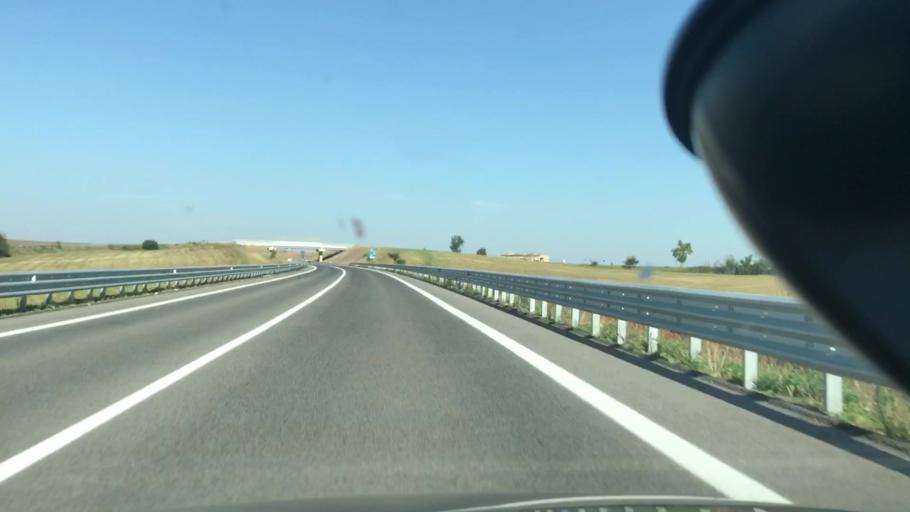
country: IT
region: Basilicate
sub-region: Provincia di Potenza
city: Palazzo San Gervasio
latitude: 40.9659
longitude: 16.0083
